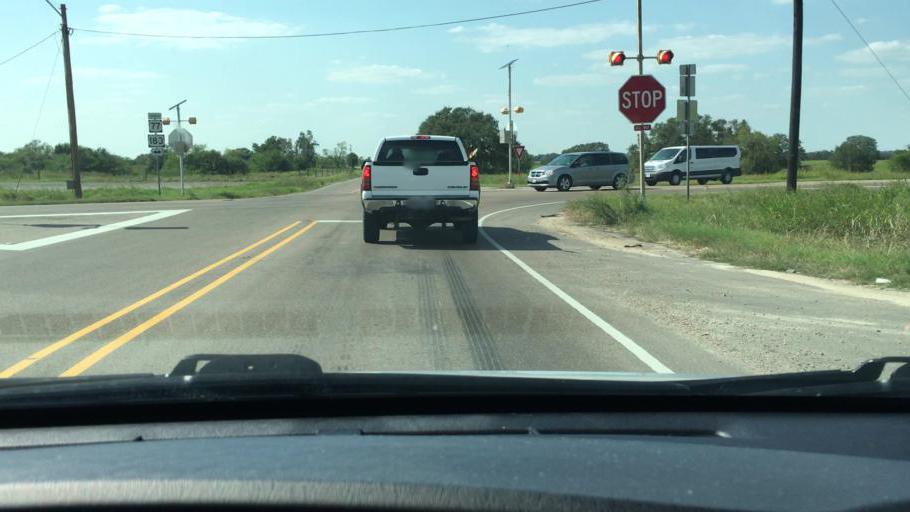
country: US
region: Texas
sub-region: DeWitt County
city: Yorktown
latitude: 28.9198
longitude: -97.3459
